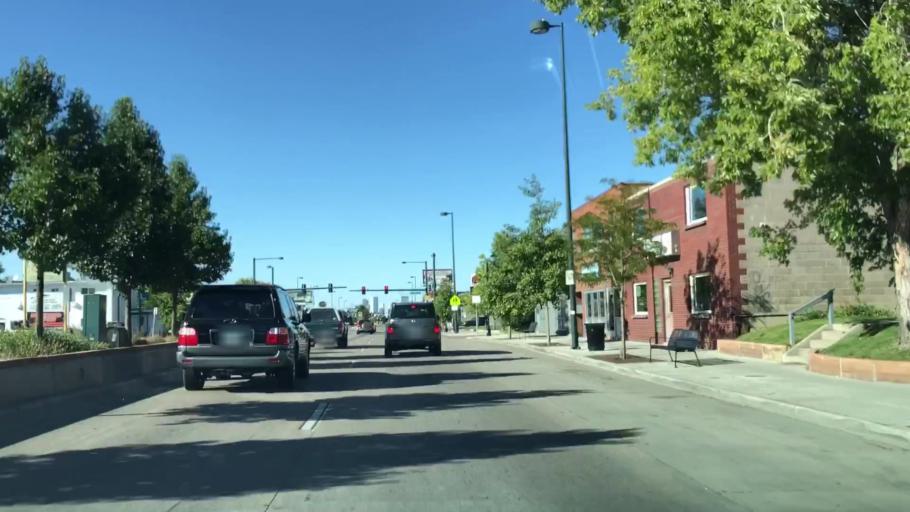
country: US
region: Colorado
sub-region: Arapahoe County
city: Englewood
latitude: 39.6737
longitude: -104.9875
